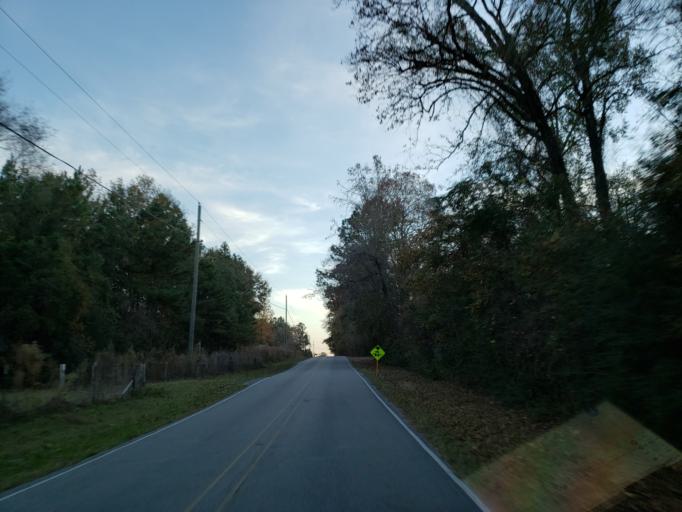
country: US
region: Mississippi
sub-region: Forrest County
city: Hattiesburg
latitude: 31.2545
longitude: -89.3141
